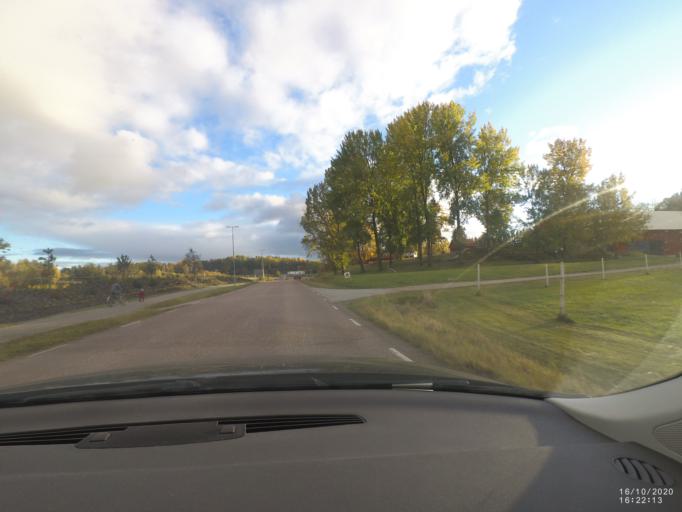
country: SE
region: Soedermanland
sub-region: Nykopings Kommun
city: Nykoping
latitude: 58.7734
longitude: 17.0061
